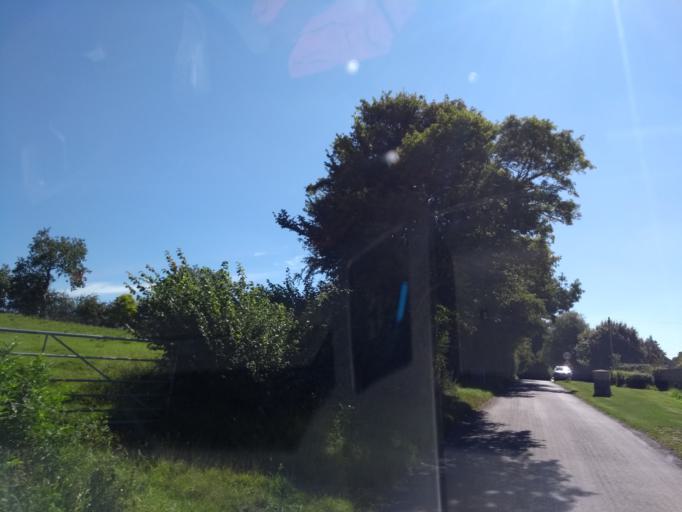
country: GB
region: England
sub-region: Somerset
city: Ilchester
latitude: 51.0528
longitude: -2.6805
